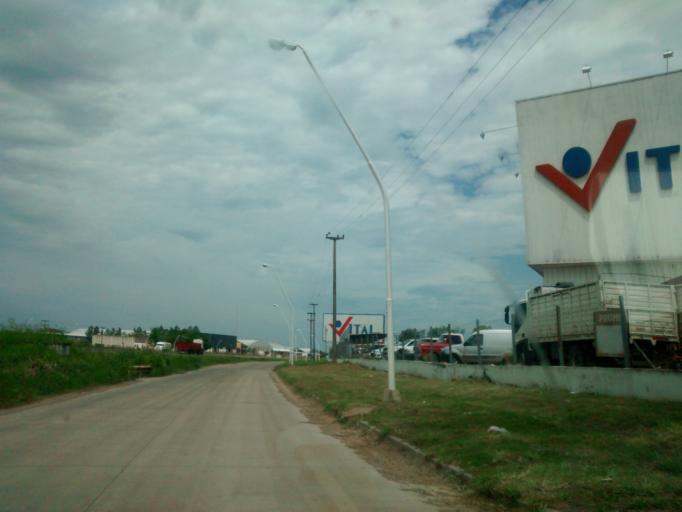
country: AR
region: Chaco
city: Fontana
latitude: -27.4089
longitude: -58.9827
